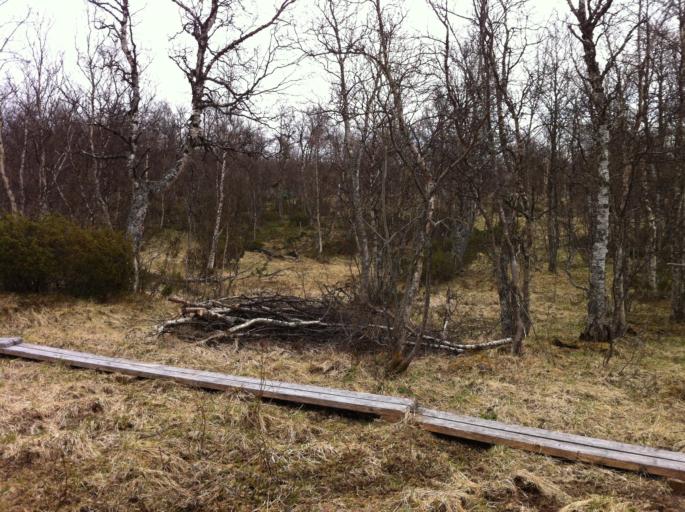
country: NO
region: Sor-Trondelag
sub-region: Tydal
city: Aas
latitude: 62.5549
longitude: 12.3125
